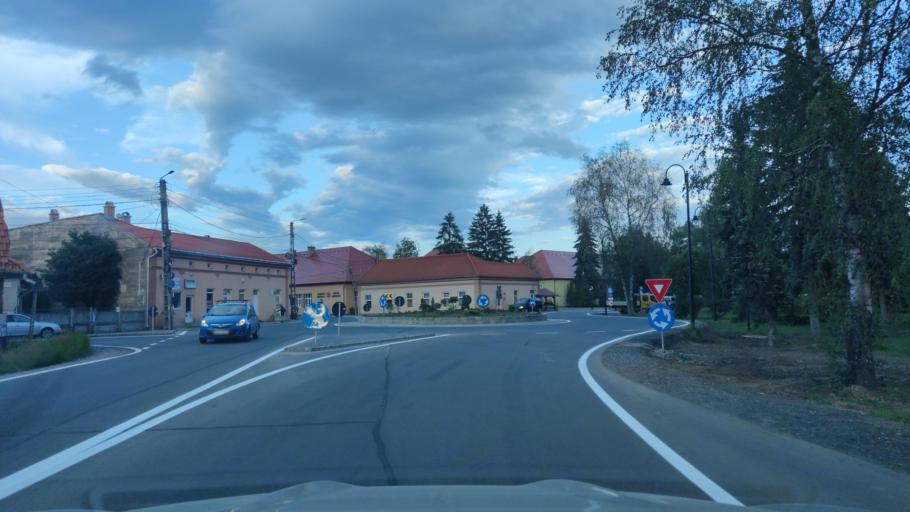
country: RO
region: Harghita
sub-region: Comuna Joseni
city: Joseni
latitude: 46.7018
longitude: 25.5036
